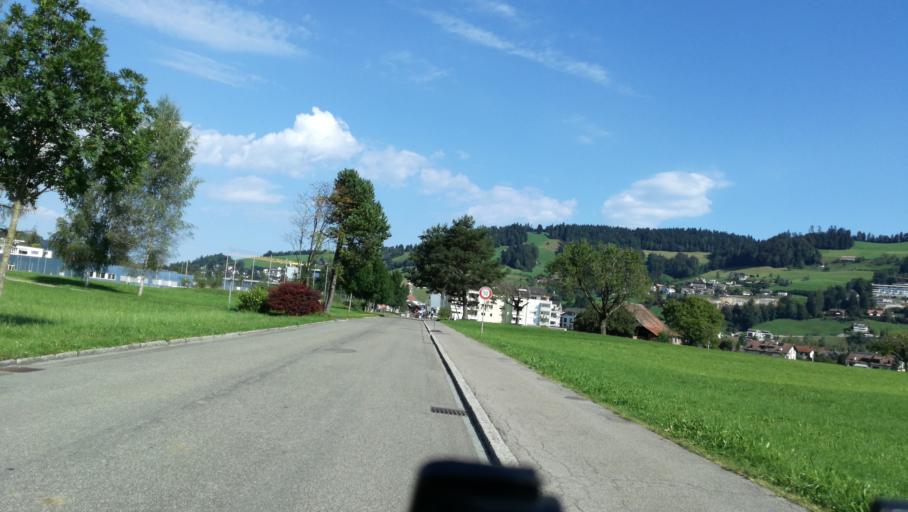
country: CH
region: Zug
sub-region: Zug
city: Unterageri
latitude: 47.1300
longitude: 8.5885
